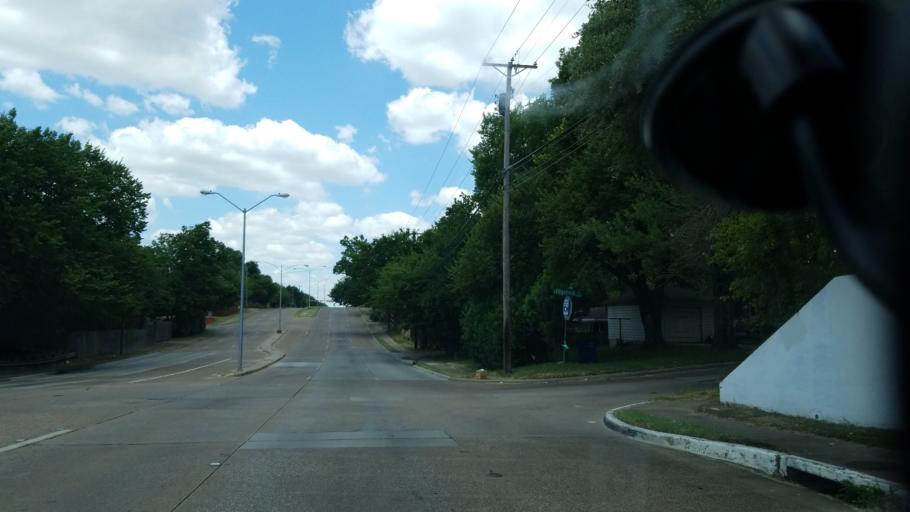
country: US
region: Texas
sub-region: Dallas County
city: Cockrell Hill
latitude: 32.7059
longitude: -96.8440
